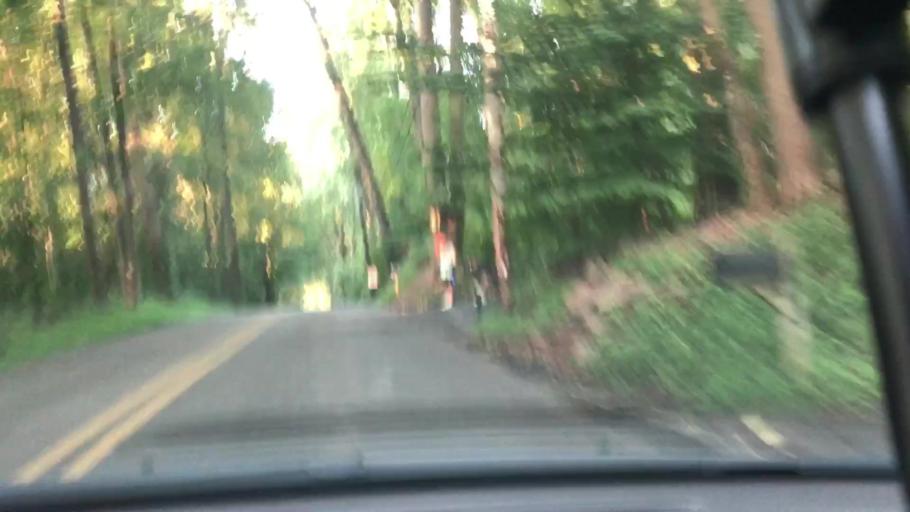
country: US
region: Pennsylvania
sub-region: Chester County
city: Kenilworth
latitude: 40.1941
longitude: -75.6455
